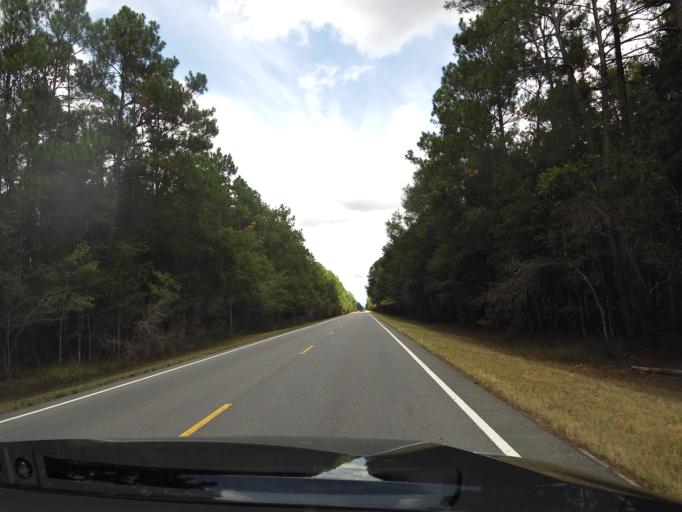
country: US
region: Georgia
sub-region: Charlton County
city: Folkston
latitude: 31.0121
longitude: -82.0259
